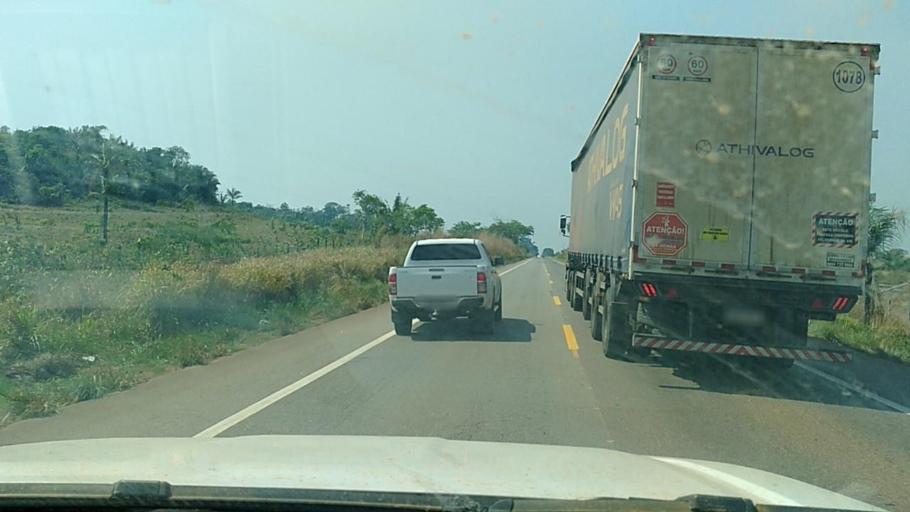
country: BR
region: Rondonia
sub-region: Porto Velho
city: Porto Velho
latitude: -8.7857
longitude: -63.4723
